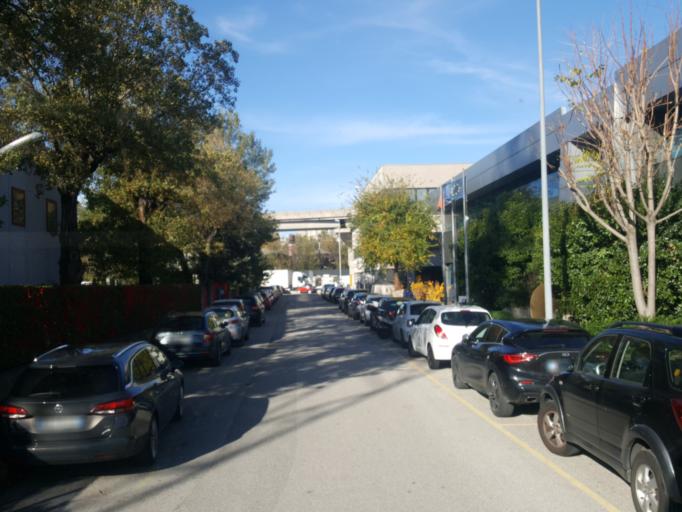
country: IT
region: Friuli Venezia Giulia
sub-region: Provincia di Trieste
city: Domio
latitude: 45.6158
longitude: 13.8064
